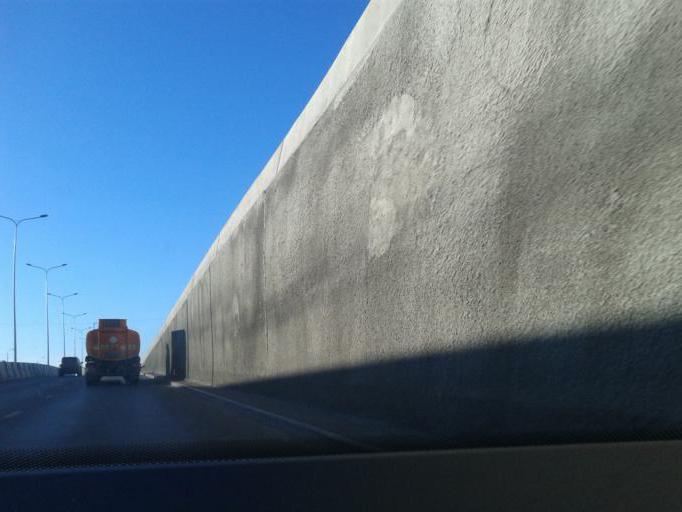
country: RU
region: Volgograd
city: Volgograd
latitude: 48.6357
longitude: 44.4300
